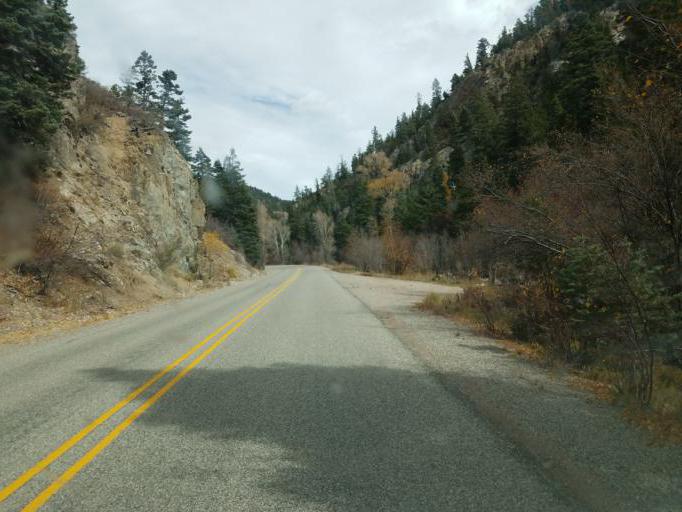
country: US
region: New Mexico
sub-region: Taos County
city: Arroyo Seco
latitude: 36.5629
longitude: -105.5271
